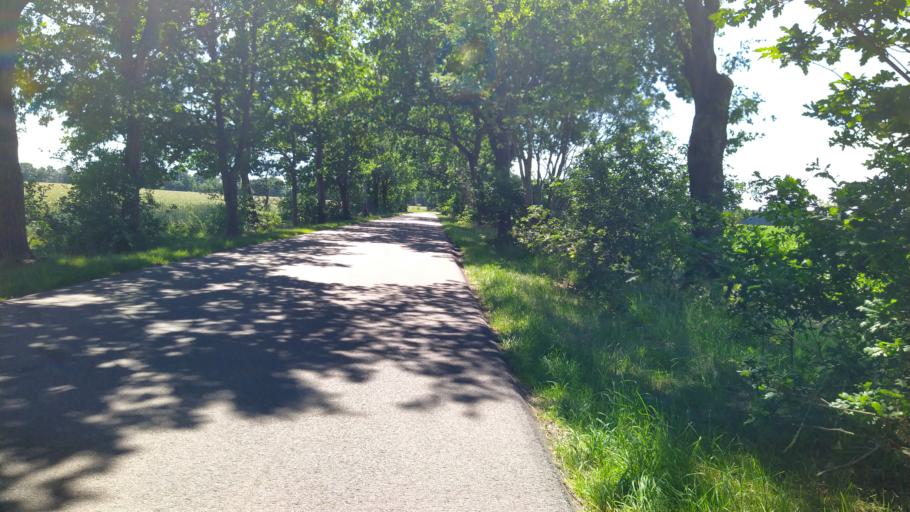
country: DE
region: Lower Saxony
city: Oldendorf
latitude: 53.5665
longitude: 9.2454
